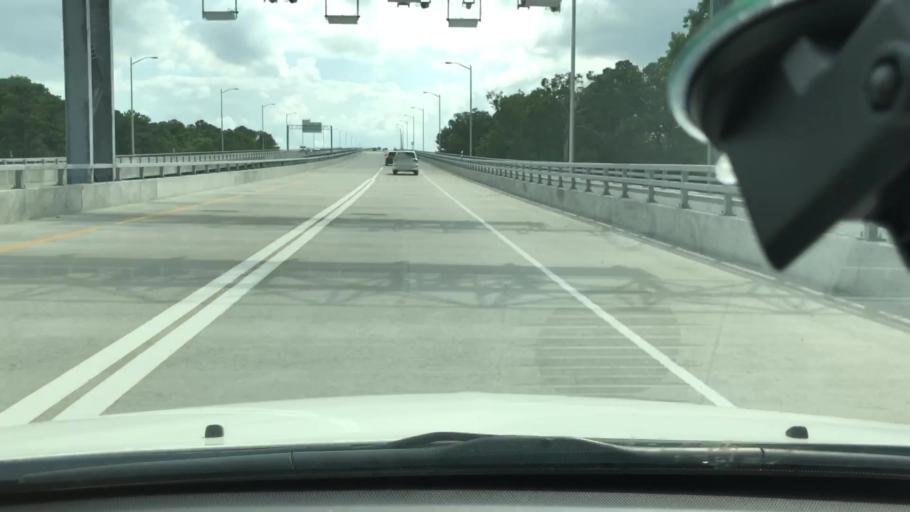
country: US
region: Virginia
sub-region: City of Chesapeake
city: Chesapeake
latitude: 36.7423
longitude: -76.2895
